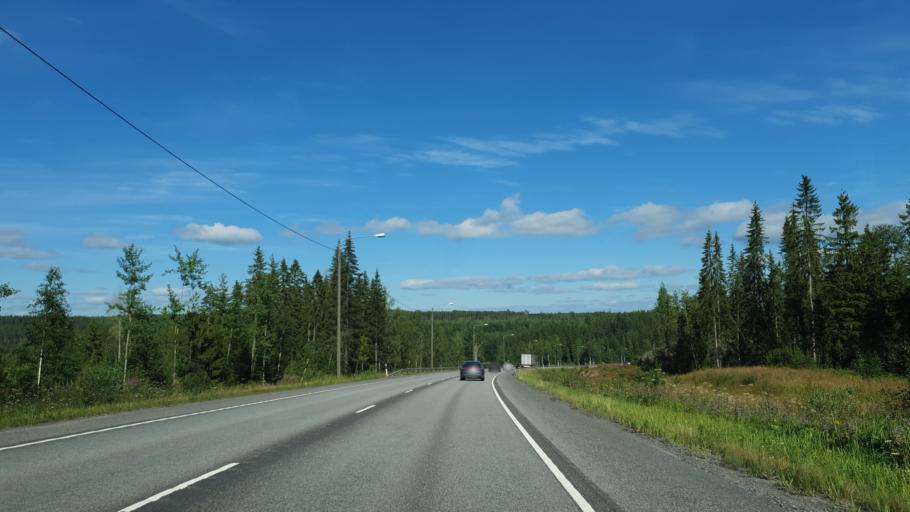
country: FI
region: Central Finland
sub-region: Jyvaeskylae
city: Toivakka
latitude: 62.2523
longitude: 26.0645
